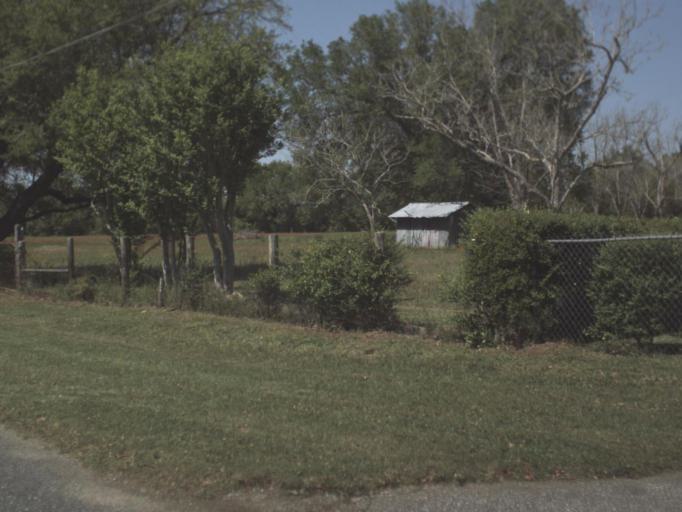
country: US
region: Florida
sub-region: Escambia County
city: Cantonment
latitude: 30.5264
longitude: -87.3902
